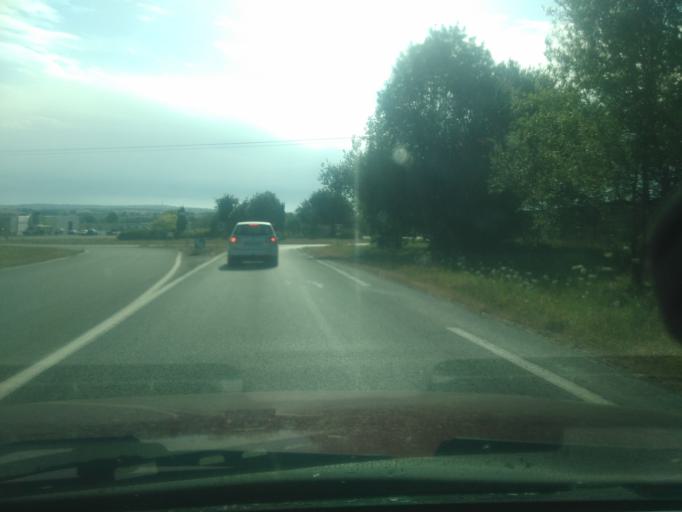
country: FR
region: Pays de la Loire
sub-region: Departement de la Vendee
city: La Chataigneraie
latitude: 46.6483
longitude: -0.7258
